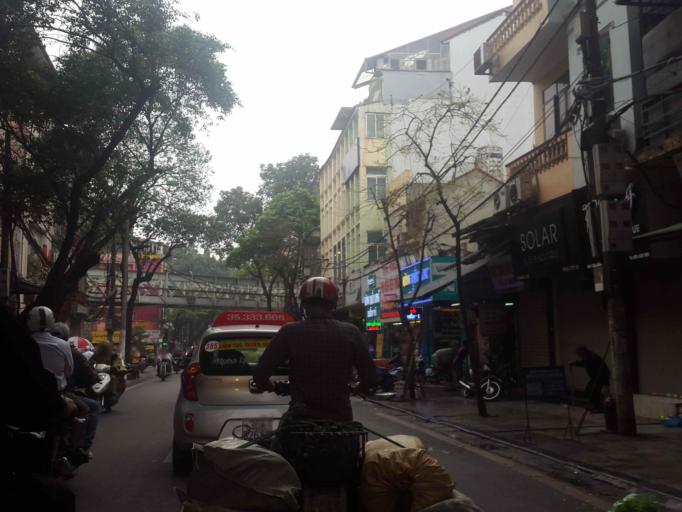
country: VN
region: Ha Noi
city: Hoan Kiem
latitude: 21.0394
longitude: 105.8471
